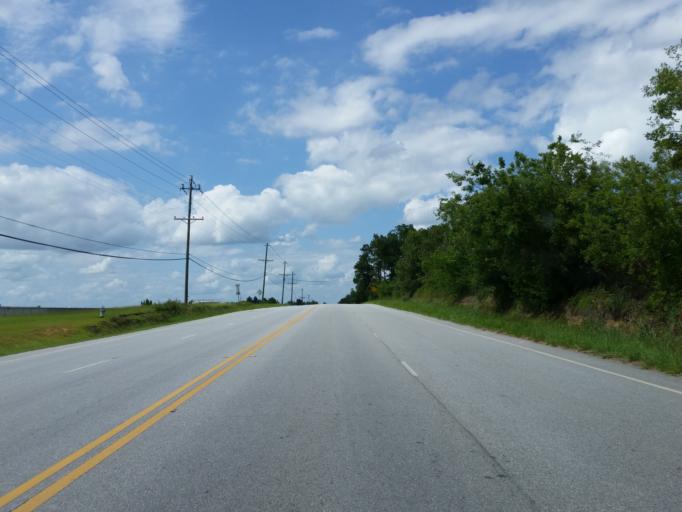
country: US
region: Georgia
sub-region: Tift County
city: Unionville
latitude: 31.4157
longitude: -83.5175
